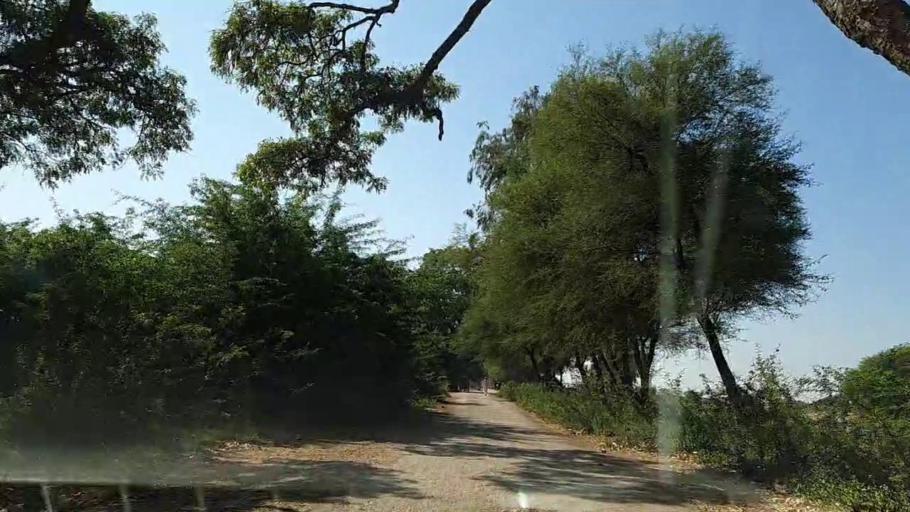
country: PK
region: Sindh
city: Chuhar Jamali
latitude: 24.5701
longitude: 68.0430
